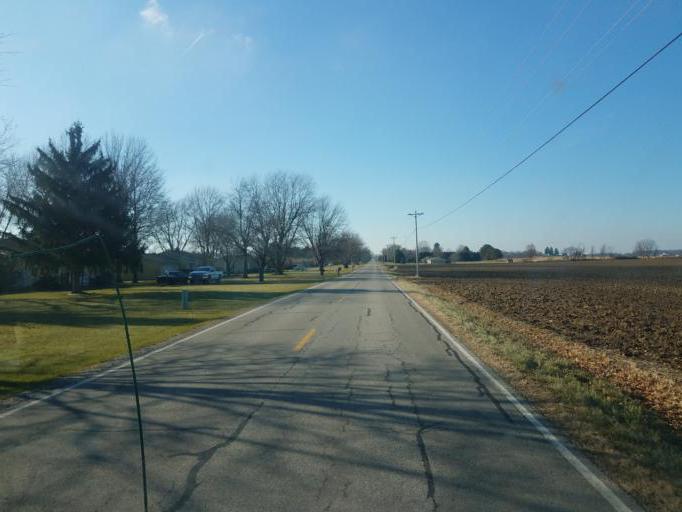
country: US
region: Ohio
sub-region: Marion County
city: Marion
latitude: 40.6447
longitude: -83.1319
